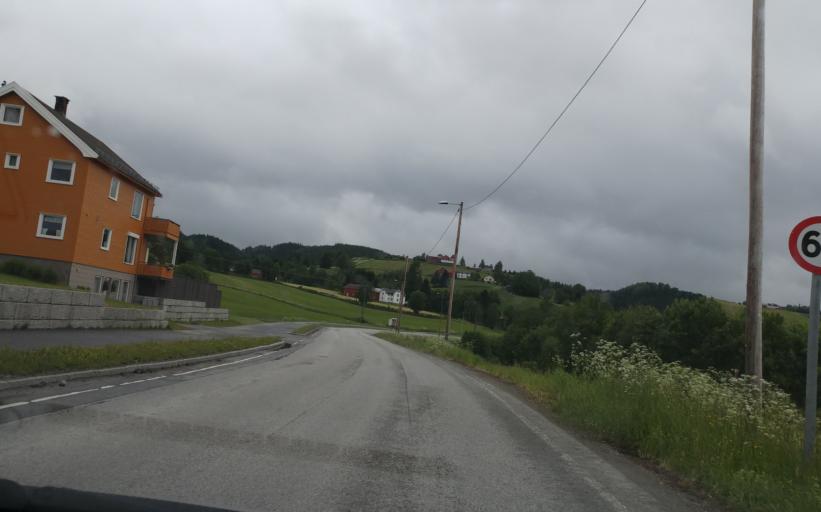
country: NO
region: Sor-Trondelag
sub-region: Selbu
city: Mebonden
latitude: 63.2466
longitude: 11.0910
